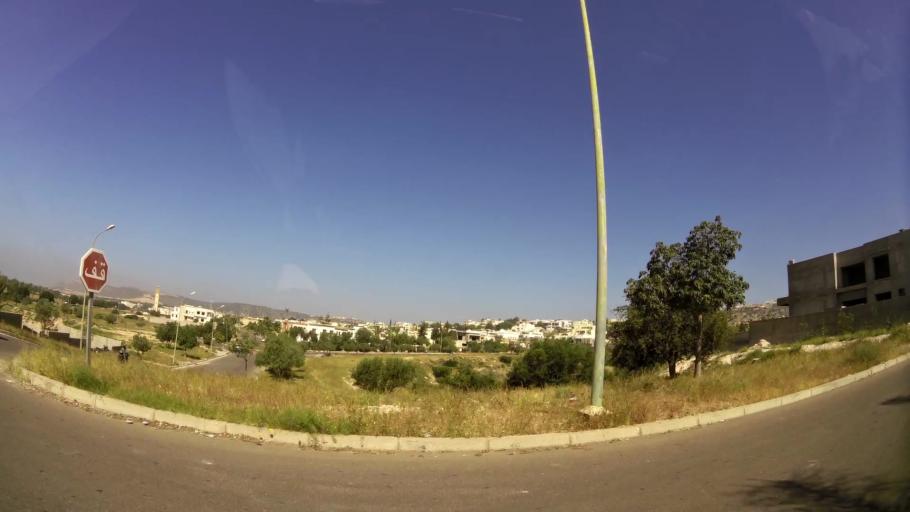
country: MA
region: Souss-Massa-Draa
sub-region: Agadir-Ida-ou-Tnan
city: Agadir
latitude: 30.4398
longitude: -9.5843
